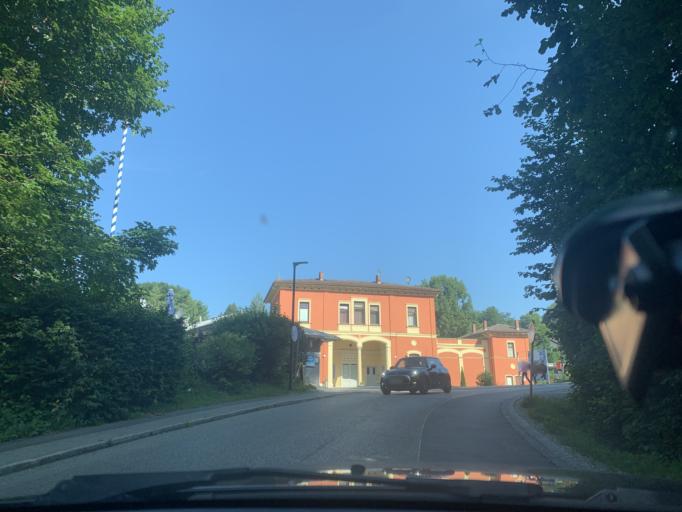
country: DE
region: Bavaria
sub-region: Upper Bavaria
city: Pocking
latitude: 47.9614
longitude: 11.3073
